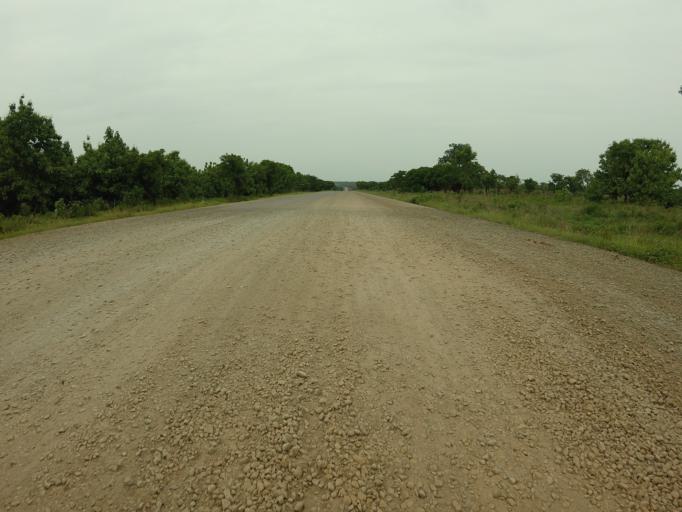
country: GH
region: Northern
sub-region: Yendi
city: Yendi
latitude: 9.2754
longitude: 0.0181
